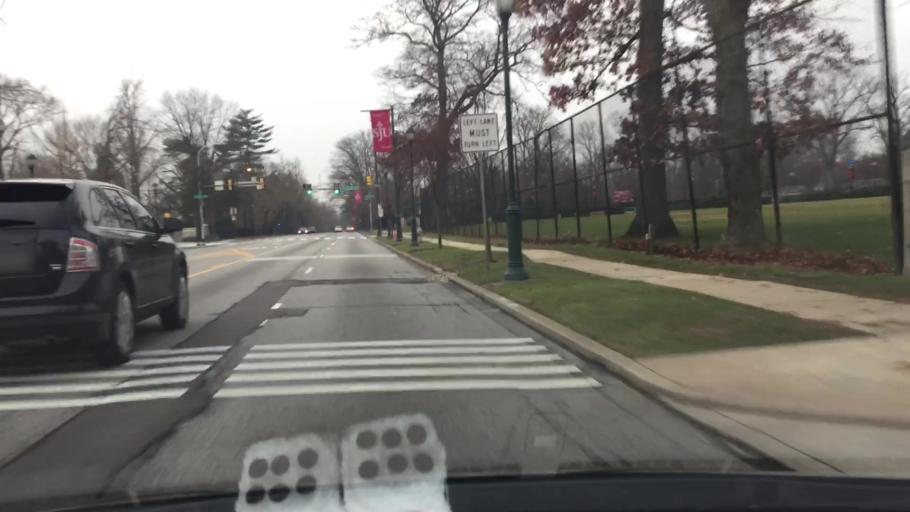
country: US
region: Pennsylvania
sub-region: Montgomery County
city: Bala-Cynwyd
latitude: 39.9946
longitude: -75.2407
